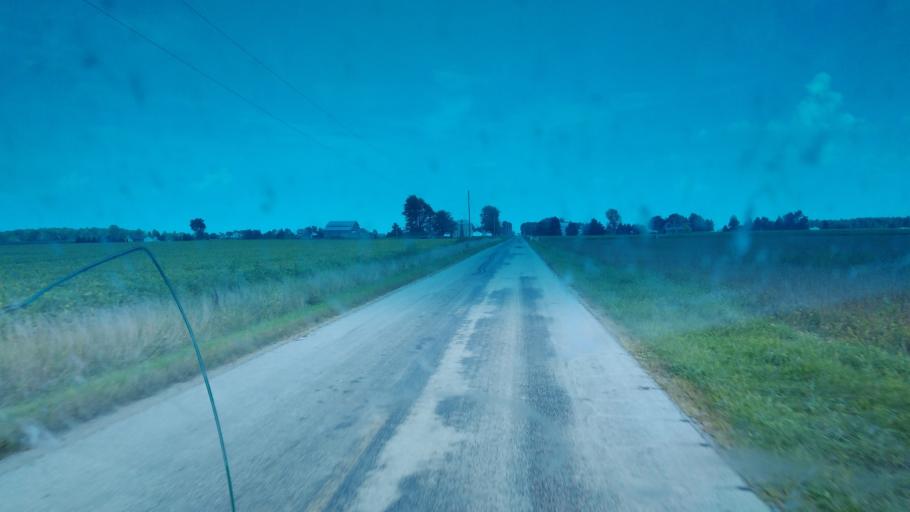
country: US
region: Ohio
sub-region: Wyandot County
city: Carey
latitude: 40.9049
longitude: -83.4745
